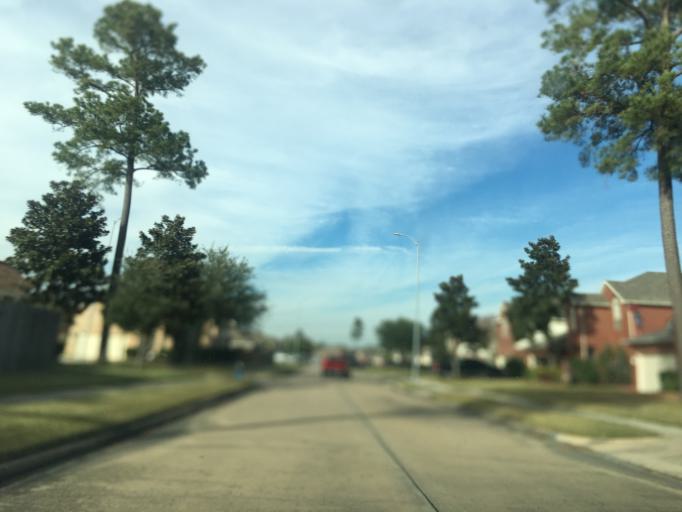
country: US
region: Texas
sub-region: Harris County
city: Cloverleaf
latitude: 29.8125
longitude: -95.1679
